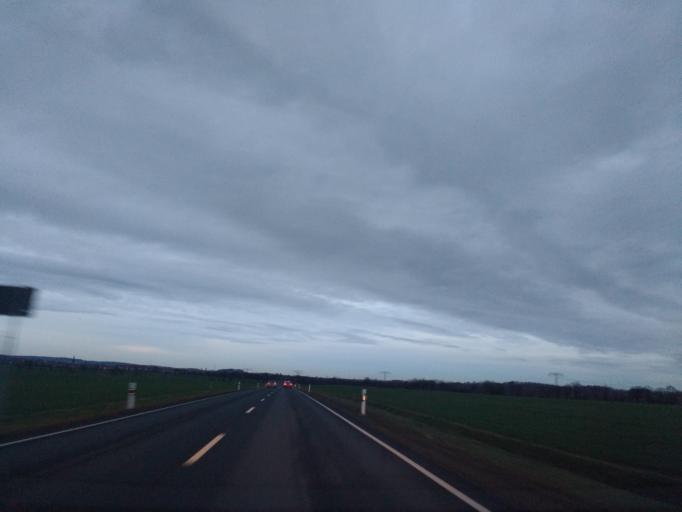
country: DE
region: Saxony-Anhalt
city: Quedlinburg
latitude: 51.7622
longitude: 11.1549
